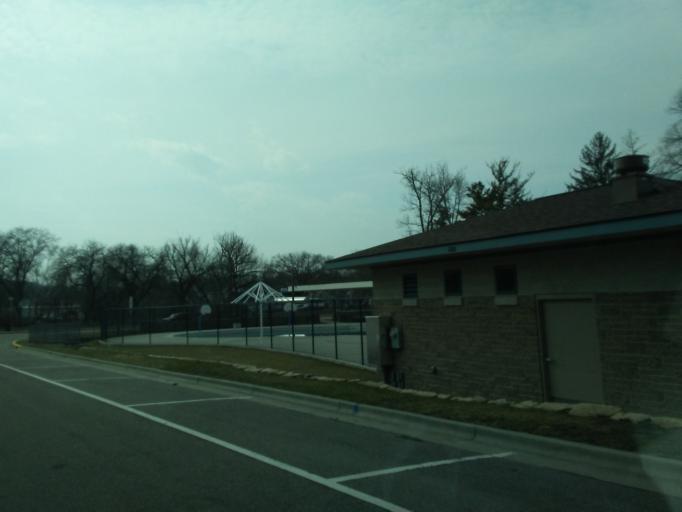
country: US
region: Wisconsin
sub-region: Columbia County
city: Lodi
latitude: 43.3177
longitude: -89.5280
